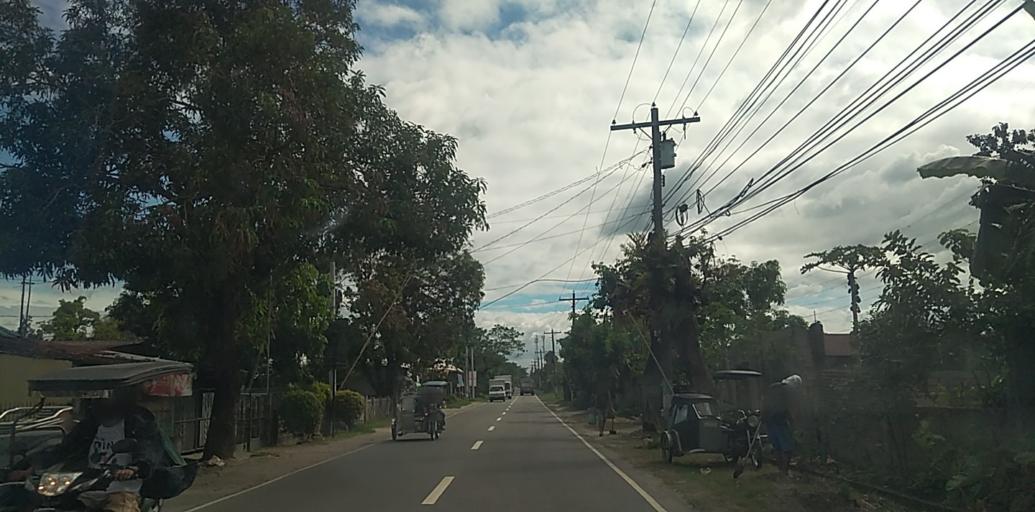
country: PH
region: Central Luzon
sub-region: Province of Pampanga
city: Buensuseso
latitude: 15.1845
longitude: 120.6759
